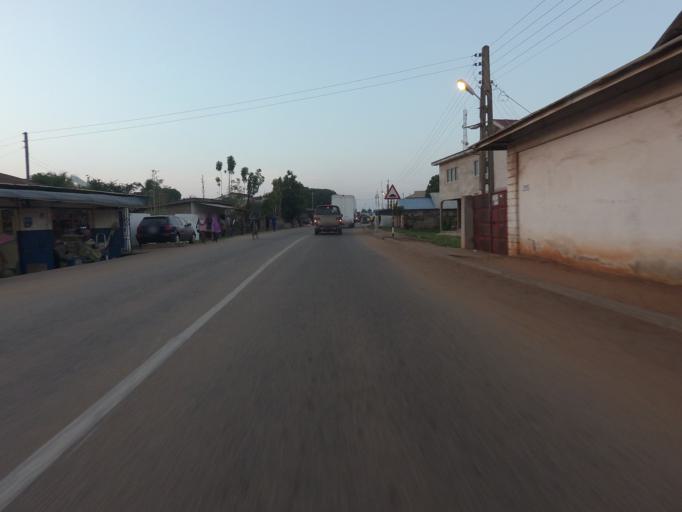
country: GH
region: Volta
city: Keta
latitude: 5.8862
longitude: 0.9827
